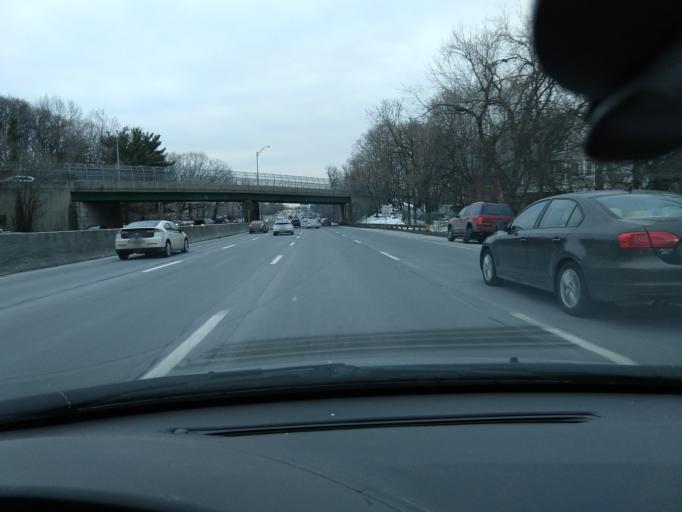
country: US
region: New Jersey
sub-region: Essex County
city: East Orange
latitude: 40.7500
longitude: -74.2124
